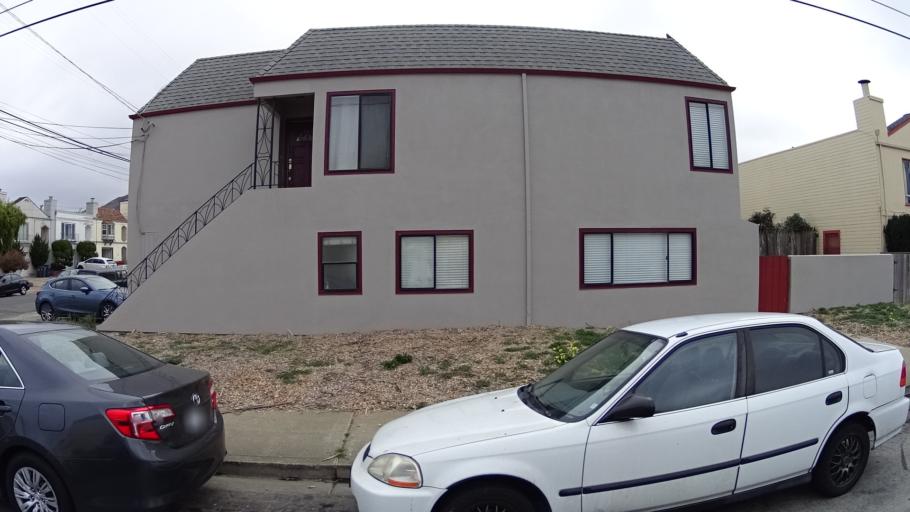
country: US
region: California
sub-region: San Mateo County
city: Colma
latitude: 37.6877
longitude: -122.4642
